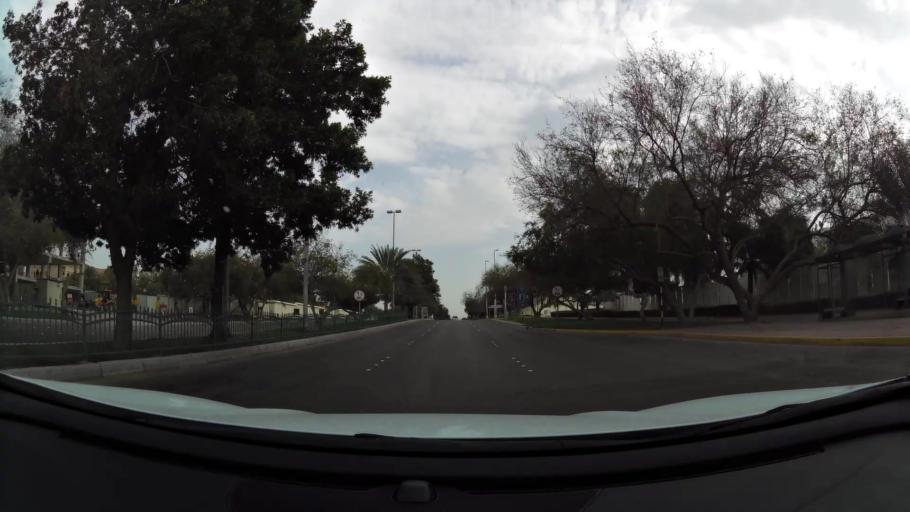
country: AE
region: Abu Dhabi
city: Abu Dhabi
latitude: 24.4661
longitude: 54.3405
